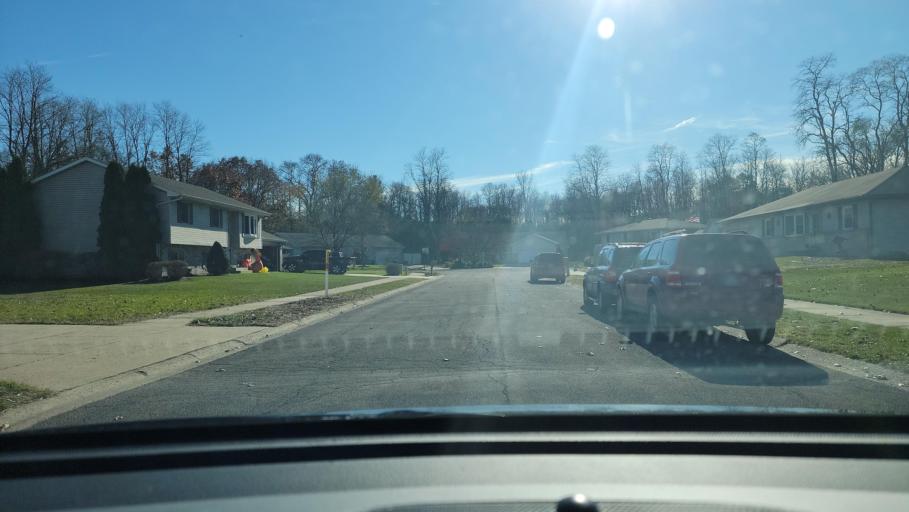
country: US
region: Indiana
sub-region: Porter County
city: Portage
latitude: 41.5868
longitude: -87.1959
